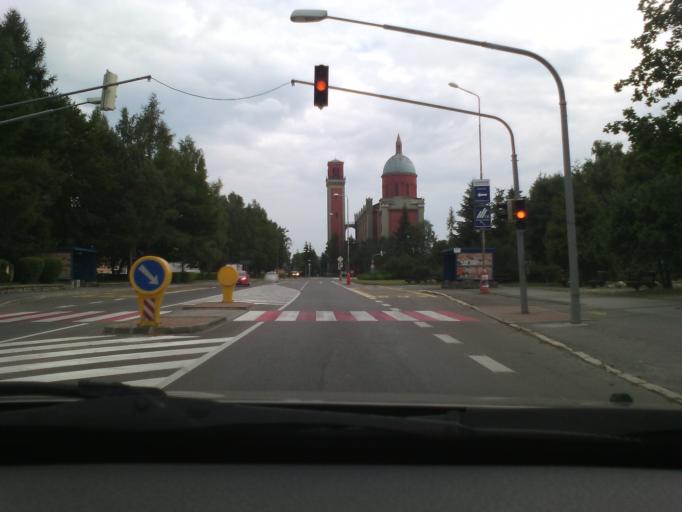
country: SK
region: Presovsky
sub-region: Okres Presov
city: Kezmarok
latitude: 49.1355
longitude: 20.4271
